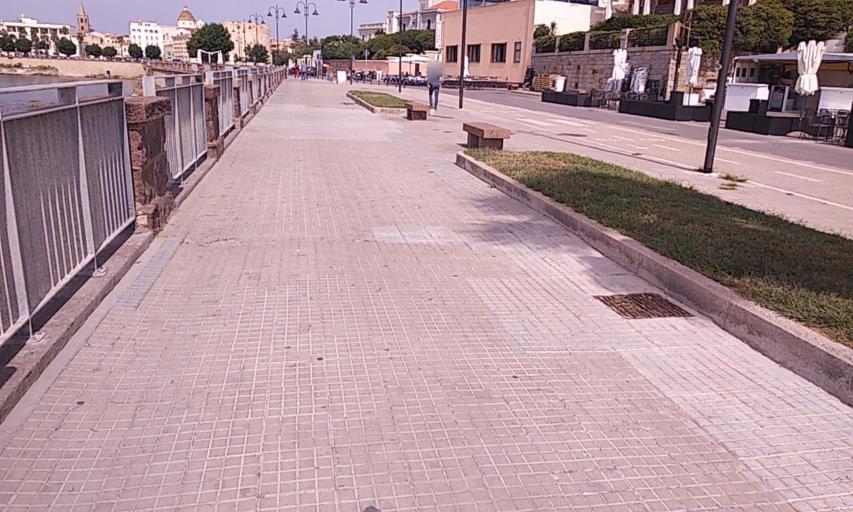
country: IT
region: Sardinia
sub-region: Provincia di Sassari
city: Alghero
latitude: 40.5533
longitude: 8.3161
